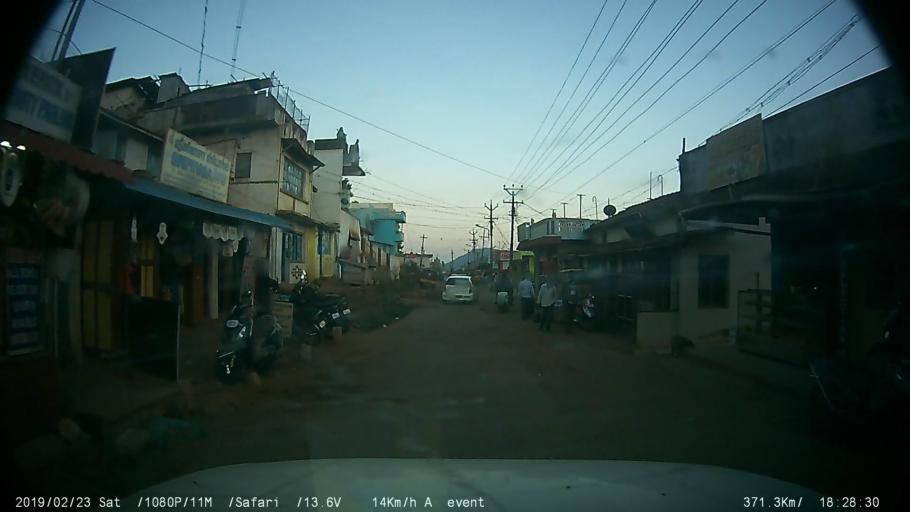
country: IN
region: Tamil Nadu
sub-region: Nilgiri
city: Wellington
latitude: 11.3487
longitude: 76.7819
